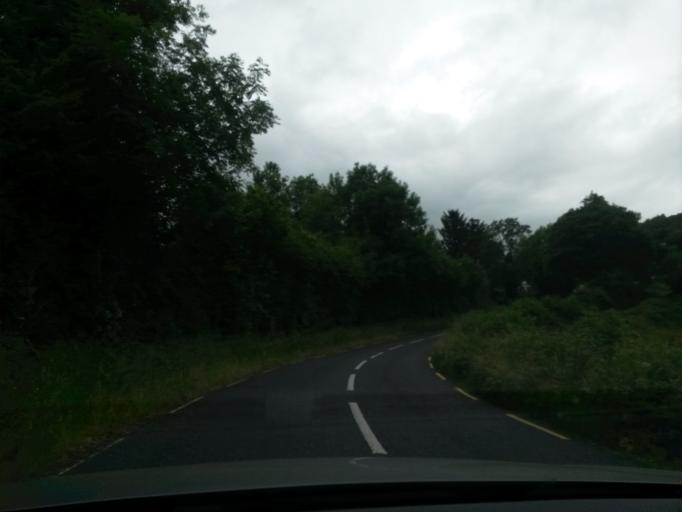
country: IE
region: Connaught
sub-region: County Leitrim
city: Manorhamilton
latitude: 54.2617
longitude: -8.3158
